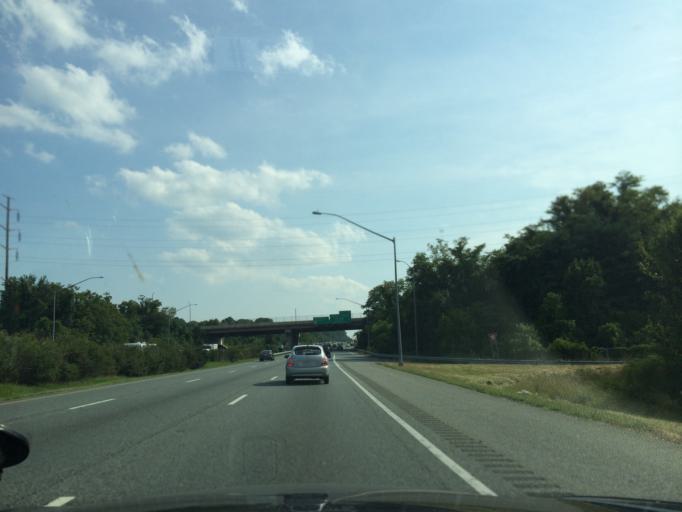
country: US
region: Maryland
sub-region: Howard County
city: Riverside
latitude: 39.2039
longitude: -76.8584
